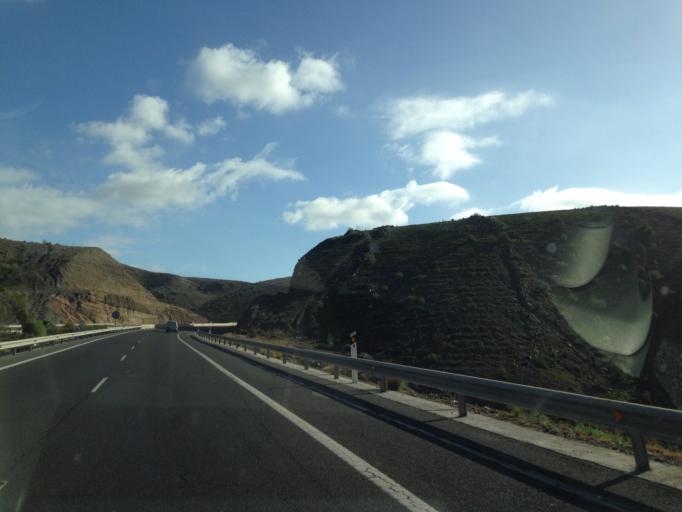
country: ES
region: Canary Islands
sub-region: Provincia de Las Palmas
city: Puerto Rico
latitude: 27.7703
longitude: -15.6574
